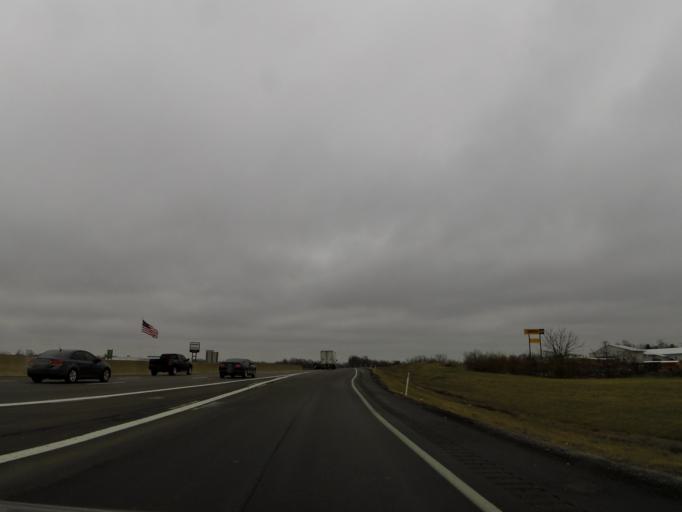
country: US
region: Kentucky
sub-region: Grant County
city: Dry Ridge
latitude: 38.6812
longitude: -84.6023
